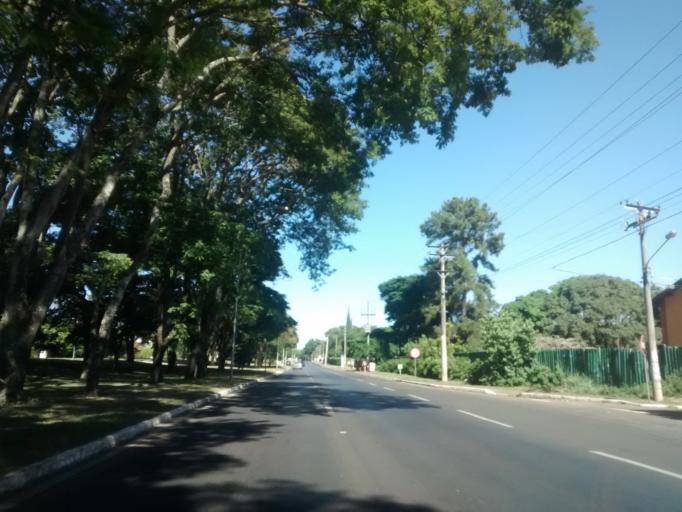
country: BR
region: Federal District
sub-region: Brasilia
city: Brasilia
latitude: -15.8480
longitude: -47.9035
